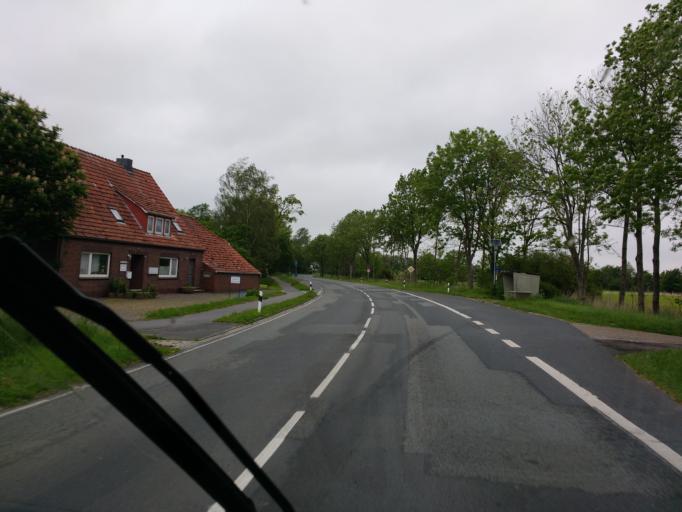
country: DE
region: Lower Saxony
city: Jever
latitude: 53.6269
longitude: 7.9274
